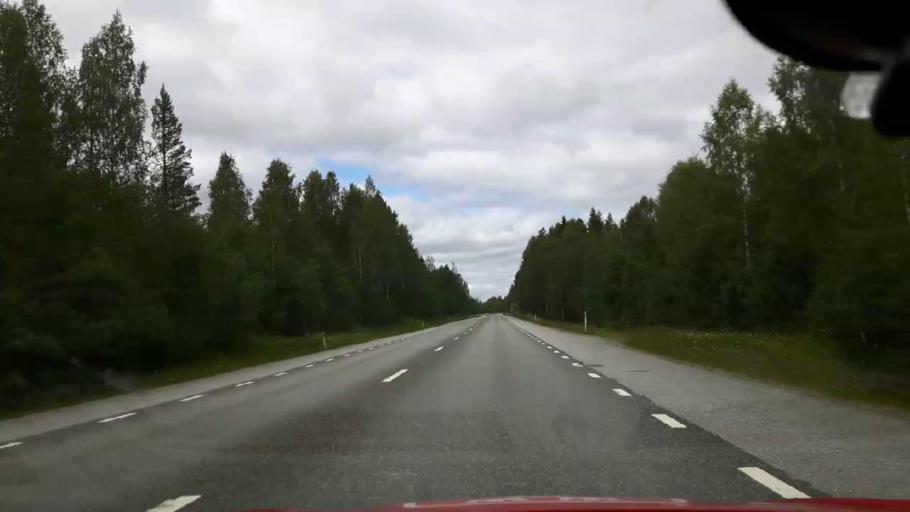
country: SE
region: Jaemtland
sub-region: Braecke Kommun
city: Braecke
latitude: 62.6968
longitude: 15.5286
